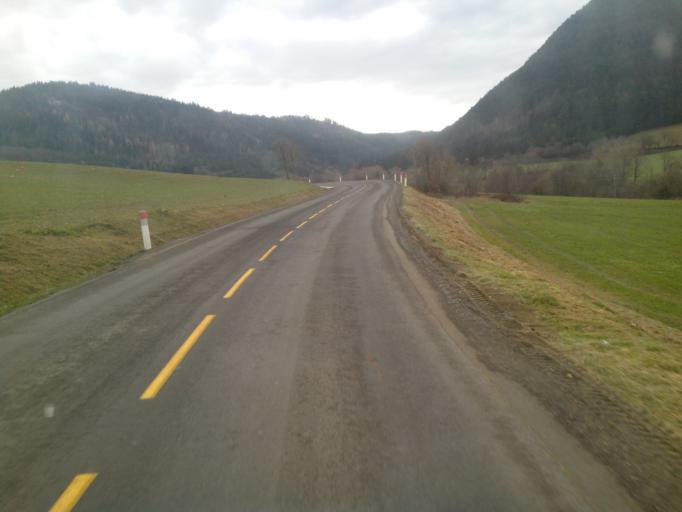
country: FR
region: Languedoc-Roussillon
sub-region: Departement de la Lozere
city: Mende
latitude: 44.4524
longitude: 3.5520
